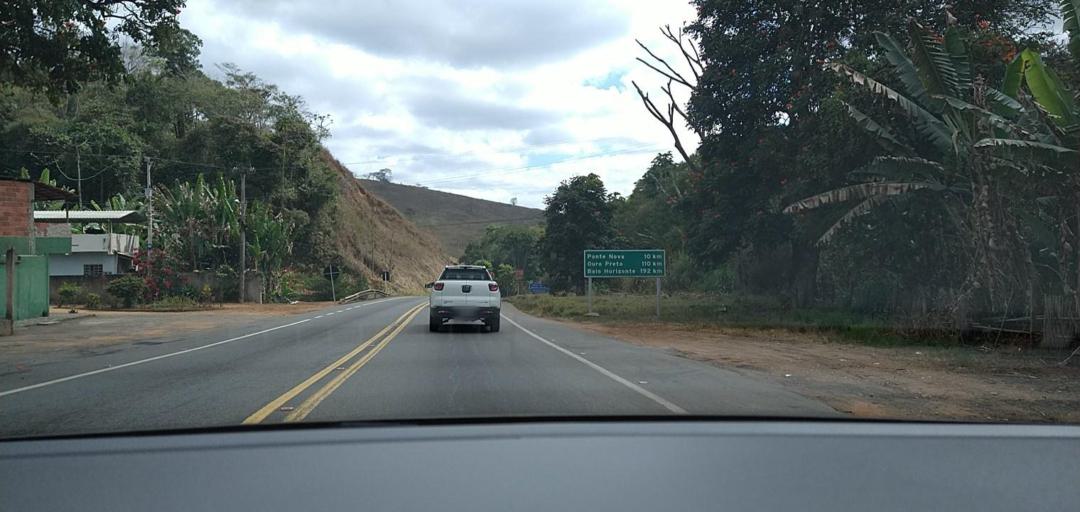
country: BR
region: Minas Gerais
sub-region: Ponte Nova
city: Ponte Nova
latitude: -20.5178
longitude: -42.8967
